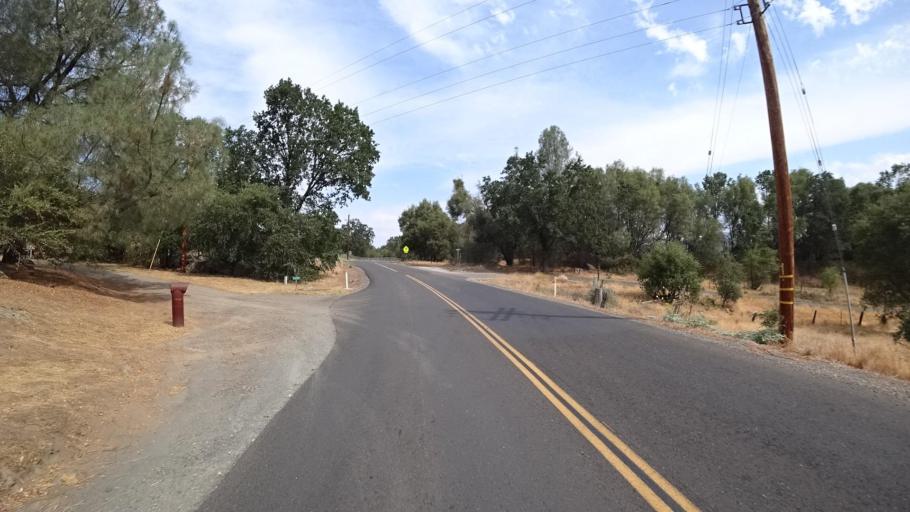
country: US
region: California
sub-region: Mariposa County
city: Mariposa
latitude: 37.4713
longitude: -119.9001
